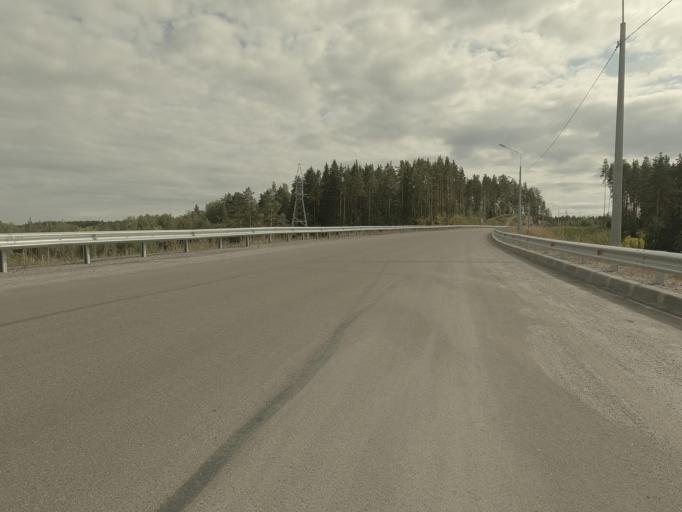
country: RU
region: Leningrad
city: Kamennogorsk
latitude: 60.9631
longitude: 29.1416
